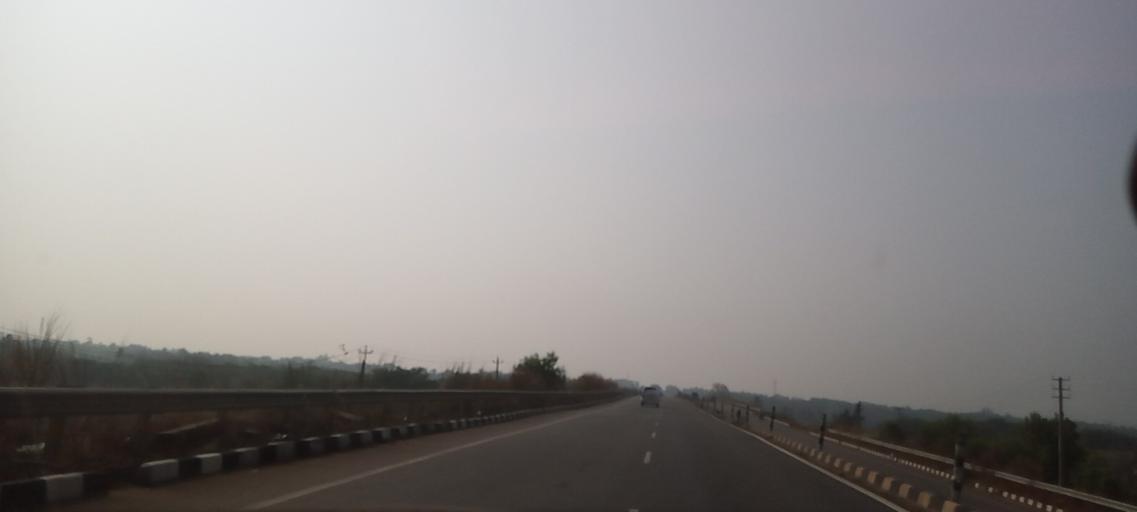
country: IN
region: Karnataka
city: Gangolli
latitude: 13.6650
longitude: 74.7051
